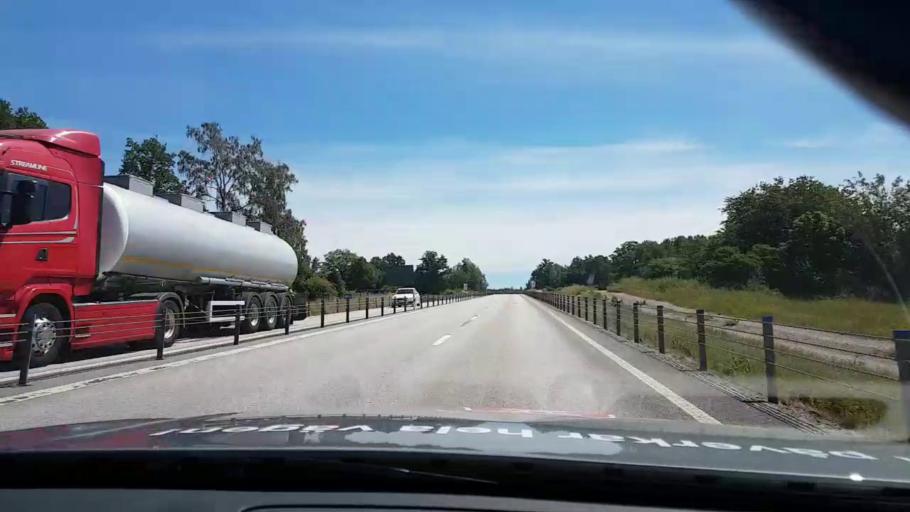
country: SE
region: Kalmar
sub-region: Vasterviks Kommun
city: Gamleby
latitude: 57.8772
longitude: 16.4004
